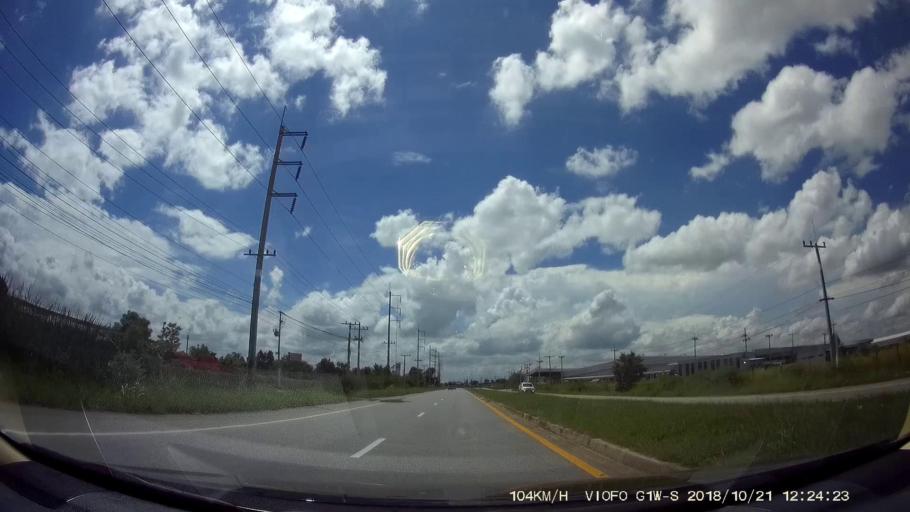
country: TH
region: Nakhon Ratchasima
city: Dan Khun Thot
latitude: 15.2338
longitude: 101.7843
